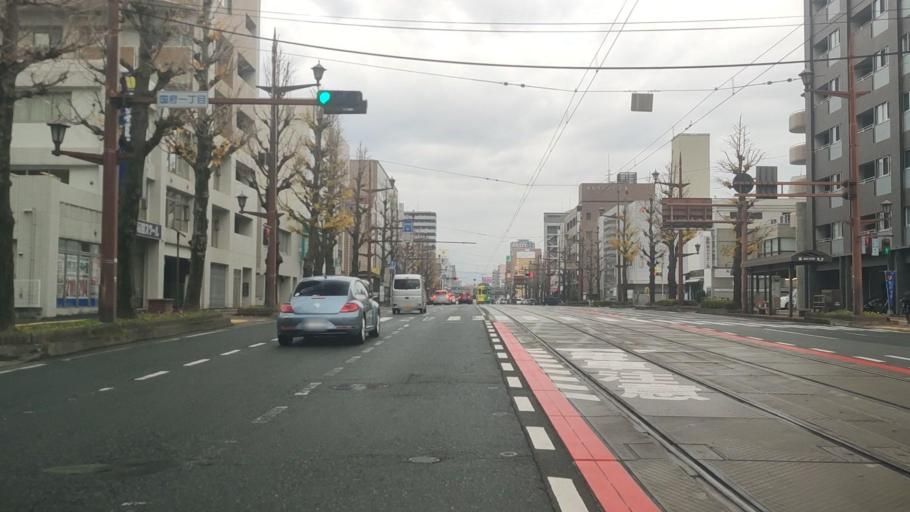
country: JP
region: Kumamoto
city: Kumamoto
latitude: 32.7910
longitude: 130.7305
